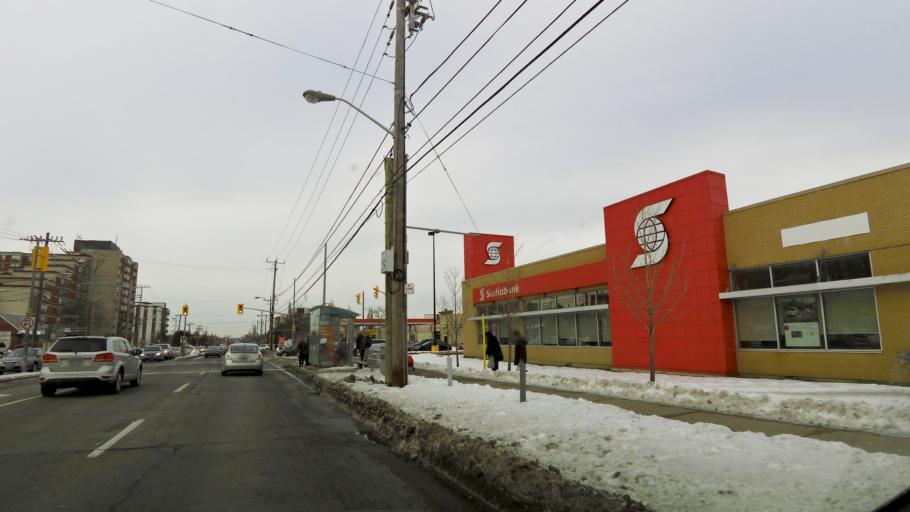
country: CA
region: Ontario
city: Etobicoke
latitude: 43.7151
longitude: -79.5550
